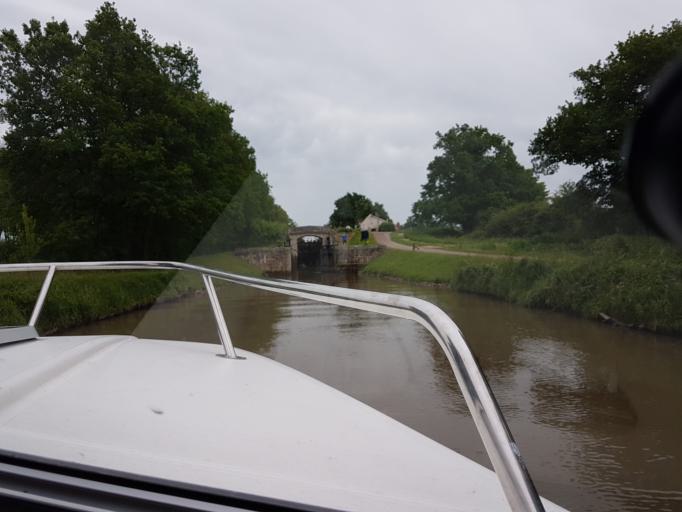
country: FR
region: Bourgogne
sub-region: Departement de la Nievre
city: Clamecy
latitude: 47.3795
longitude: 3.6033
